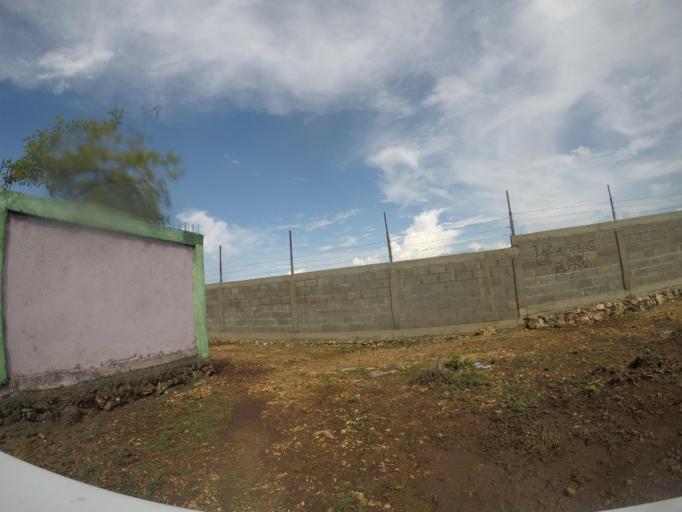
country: TL
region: Baucau
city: Baucau
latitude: -8.4801
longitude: 126.4552
